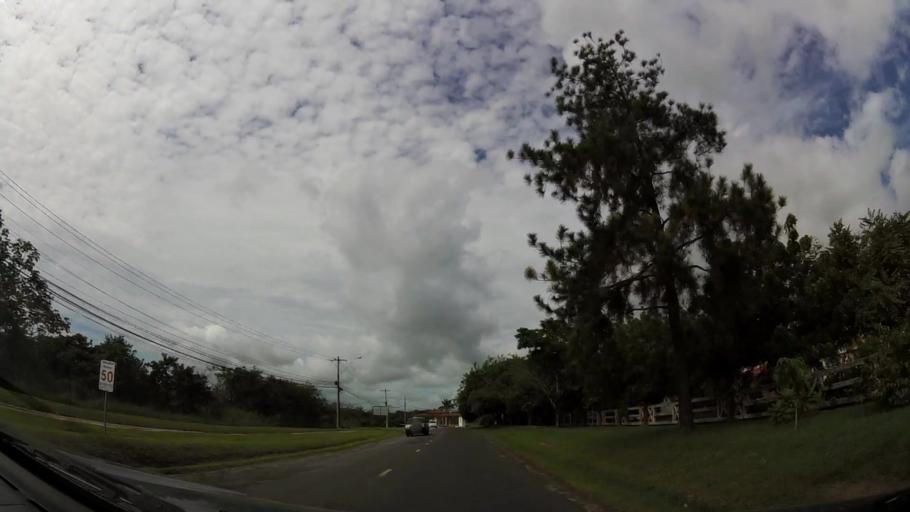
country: PA
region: Panama
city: Nueva Gorgona
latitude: 8.5372
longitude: -79.9039
